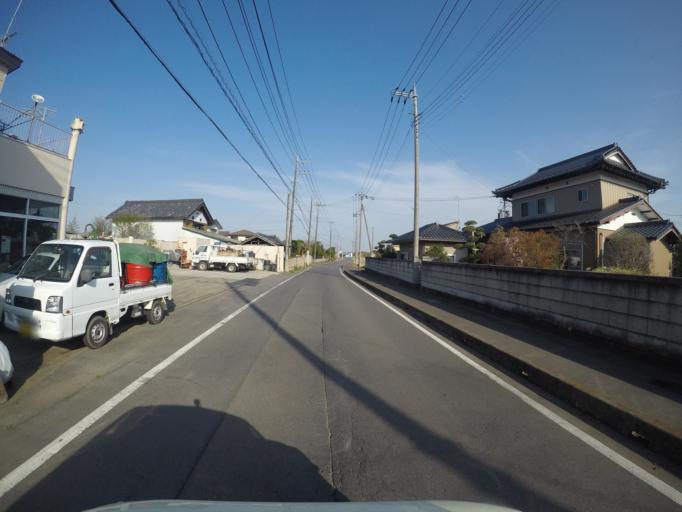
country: JP
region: Ibaraki
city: Ishige
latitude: 36.1454
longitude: 140.0249
